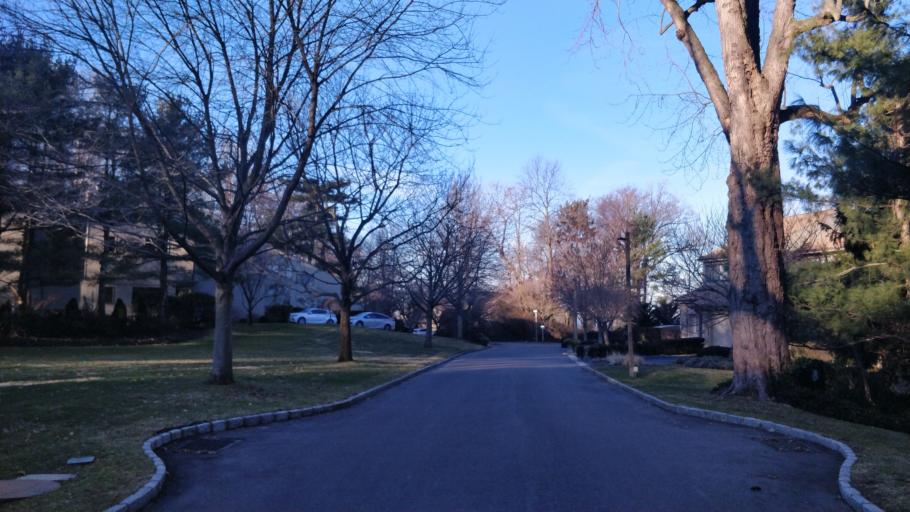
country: US
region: New York
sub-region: Nassau County
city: Glen Cove
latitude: 40.8691
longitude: -73.6505
